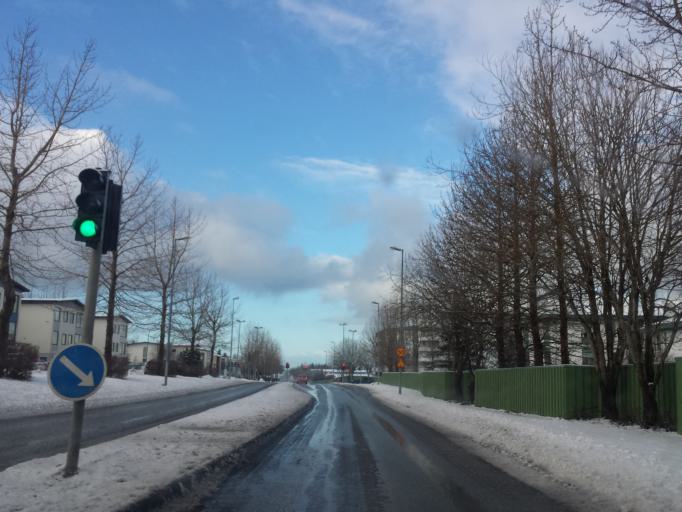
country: IS
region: Capital Region
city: Reykjavik
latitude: 64.1138
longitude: -21.8731
